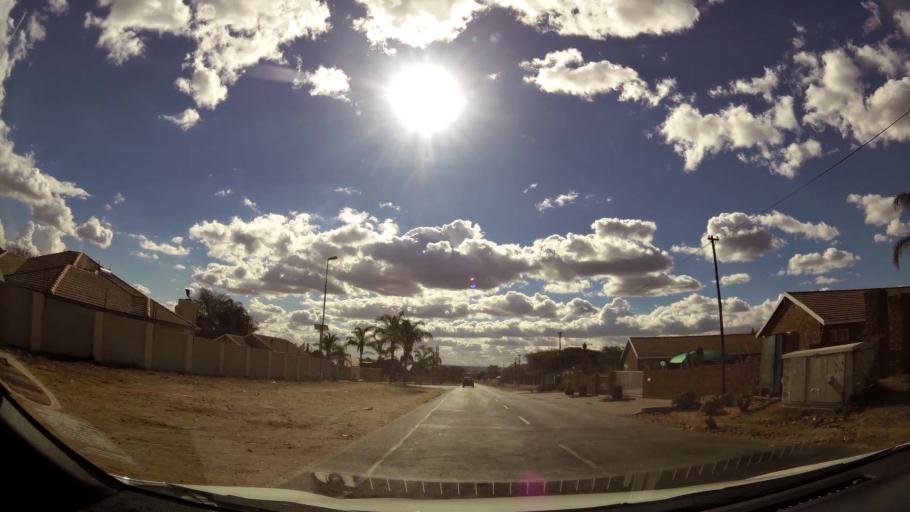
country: ZA
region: Limpopo
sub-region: Capricorn District Municipality
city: Polokwane
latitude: -23.8830
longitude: 29.4839
